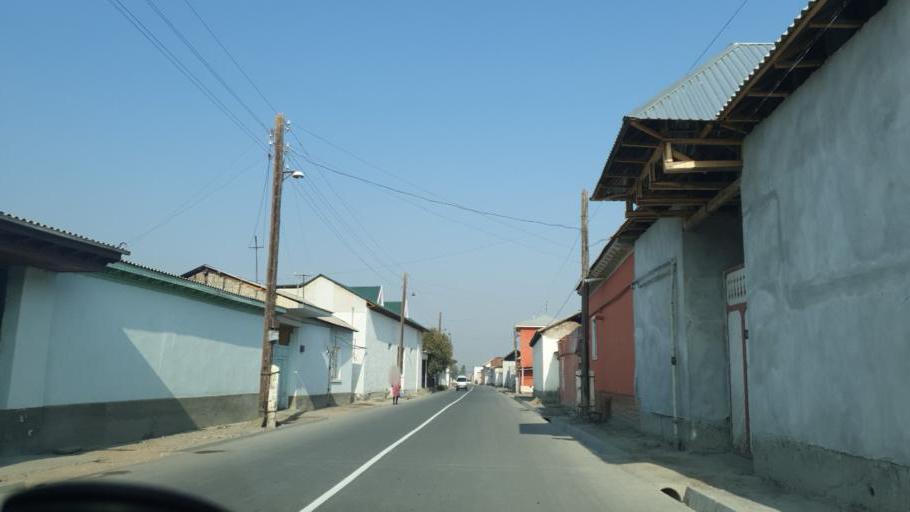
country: UZ
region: Fergana
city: Qo`qon
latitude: 40.5846
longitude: 70.9078
